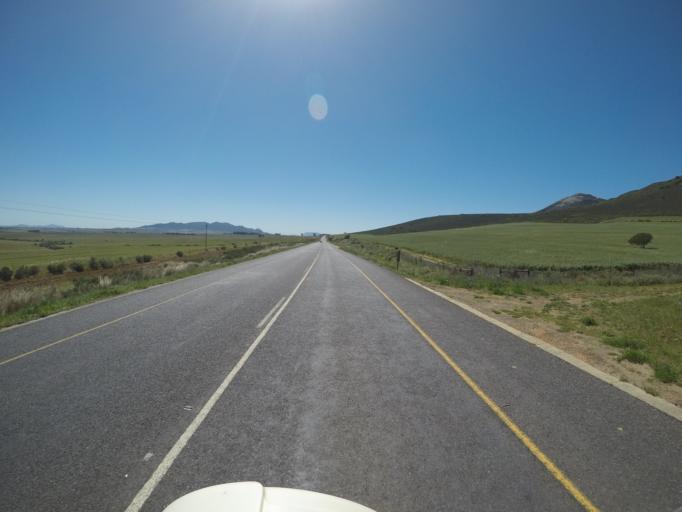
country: ZA
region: Western Cape
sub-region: Cape Winelands District Municipality
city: Noorder-Paarl
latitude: -33.7345
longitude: 18.8912
